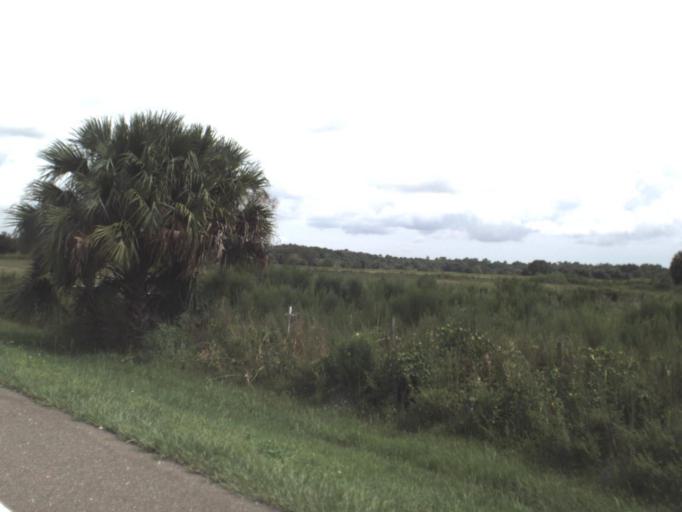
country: US
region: Florida
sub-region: Sarasota County
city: North Port
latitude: 27.1933
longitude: -82.0905
